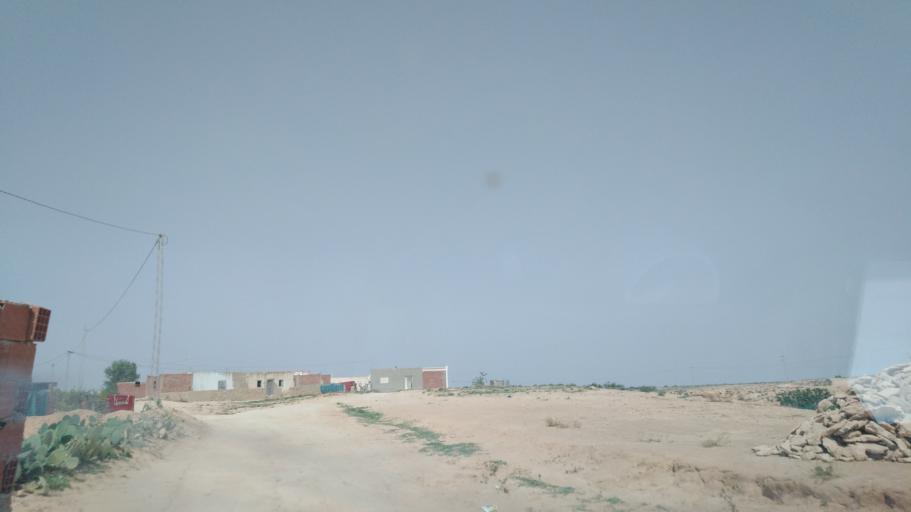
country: TN
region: Safaqis
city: Sfax
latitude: 34.6411
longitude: 10.5623
